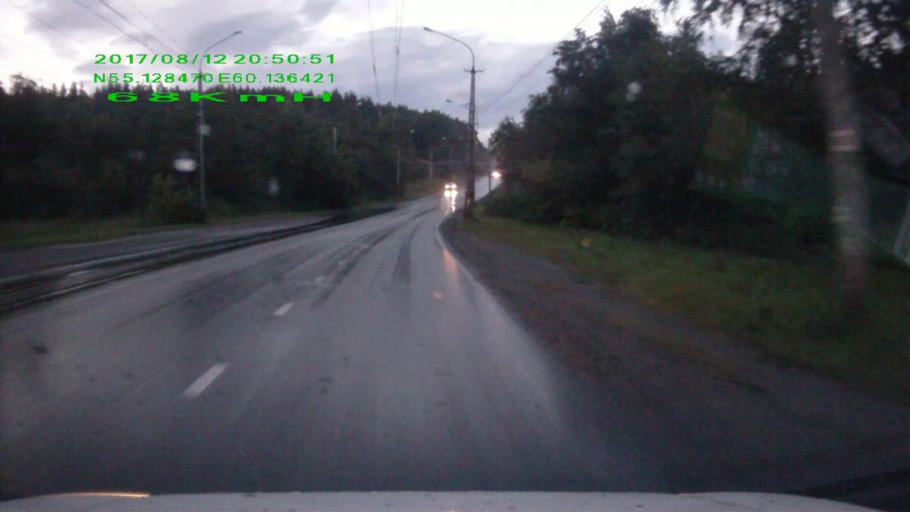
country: RU
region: Chelyabinsk
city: Turgoyak
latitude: 55.1285
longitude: 60.1365
